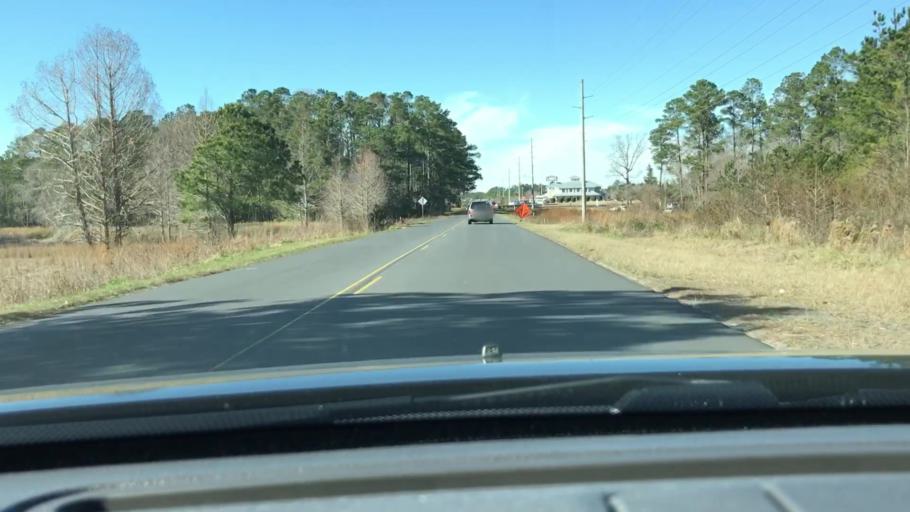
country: US
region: North Carolina
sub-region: Brunswick County
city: Shallotte
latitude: 33.9704
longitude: -78.3955
